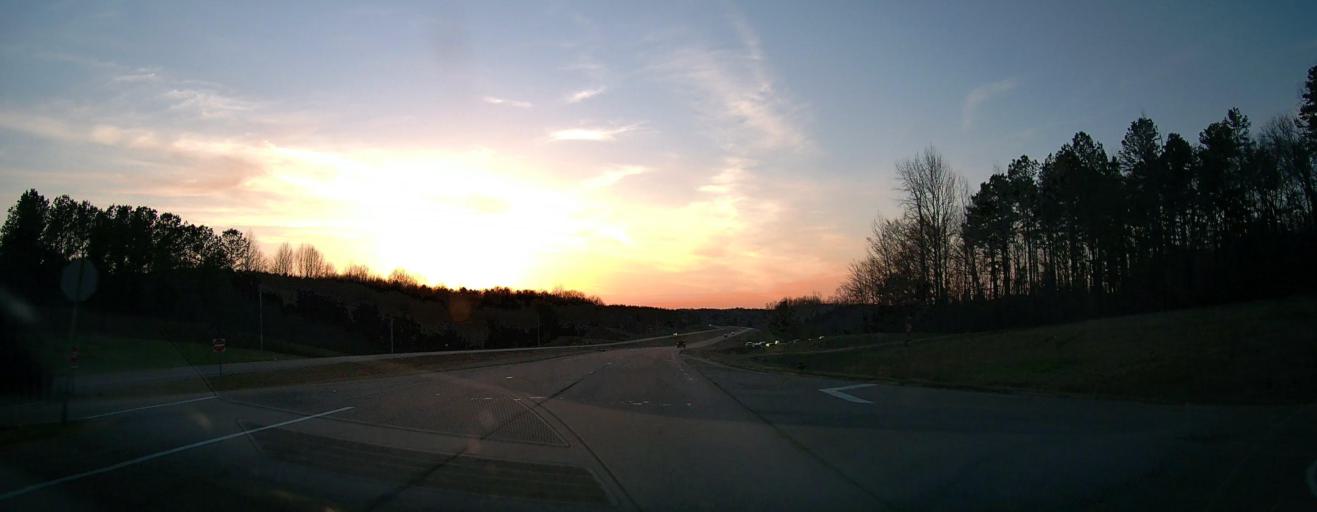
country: US
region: Mississippi
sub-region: Alcorn County
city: Corinth
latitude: 34.9319
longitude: -88.7163
